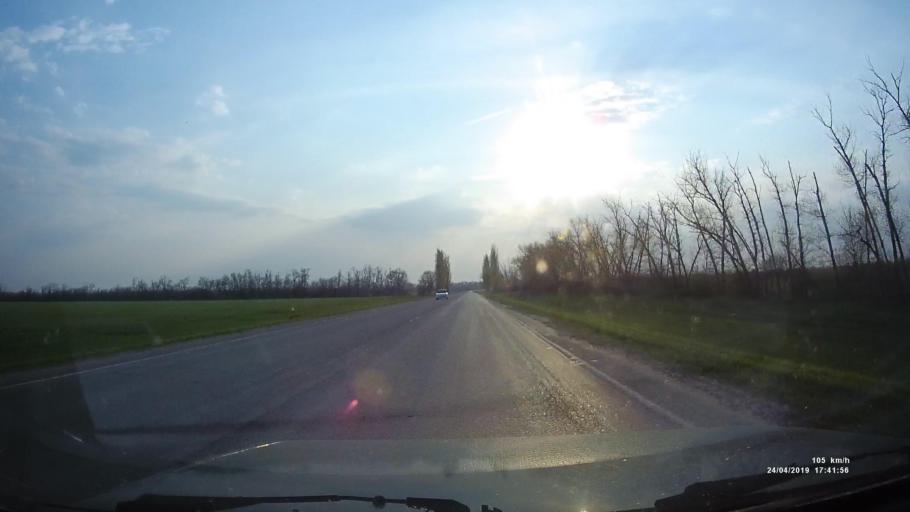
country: RU
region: Rostov
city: Tselina
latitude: 46.5307
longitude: 40.9593
